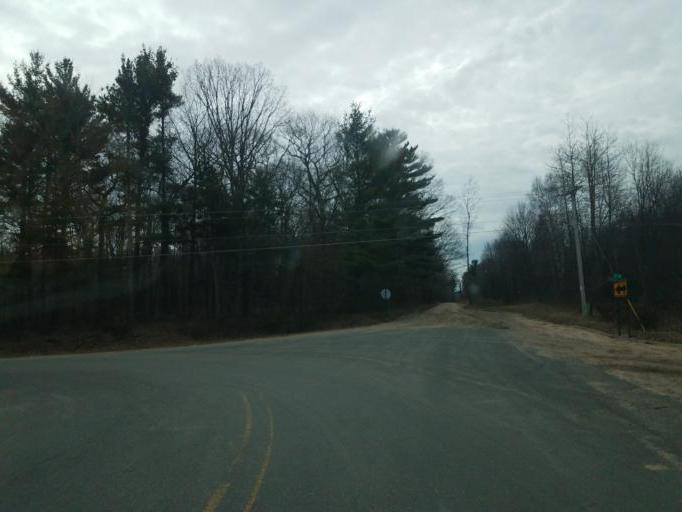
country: US
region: Michigan
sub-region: Oceana County
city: Hart
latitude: 43.6567
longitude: -86.5229
